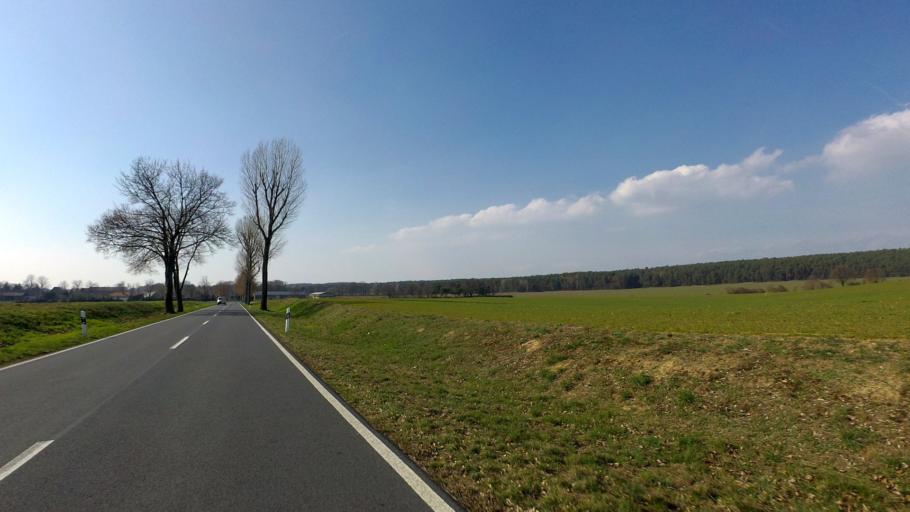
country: DE
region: Brandenburg
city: Drahnsdorf
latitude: 51.9121
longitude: 13.5268
